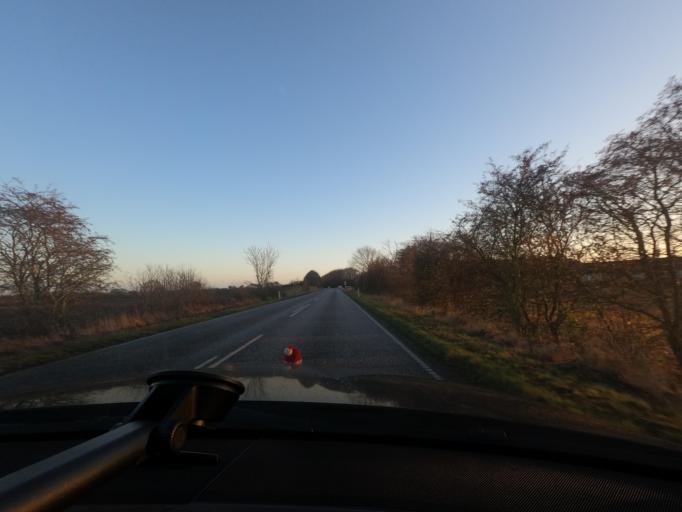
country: DK
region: South Denmark
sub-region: Sonderborg Kommune
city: Horuphav
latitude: 54.9135
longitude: 9.9114
